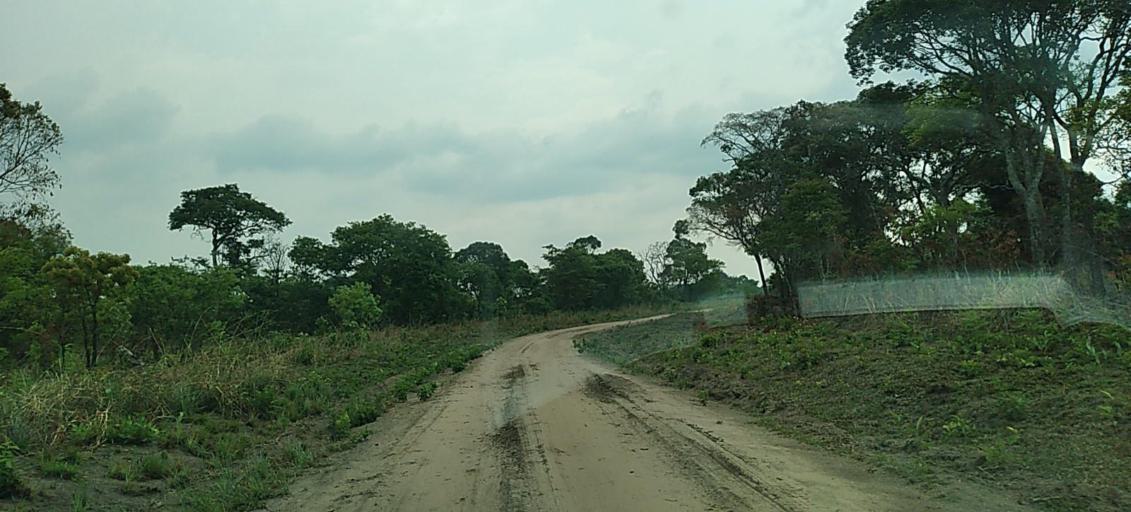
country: ZM
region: North-Western
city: Mwinilunga
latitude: -11.4064
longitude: 24.6280
